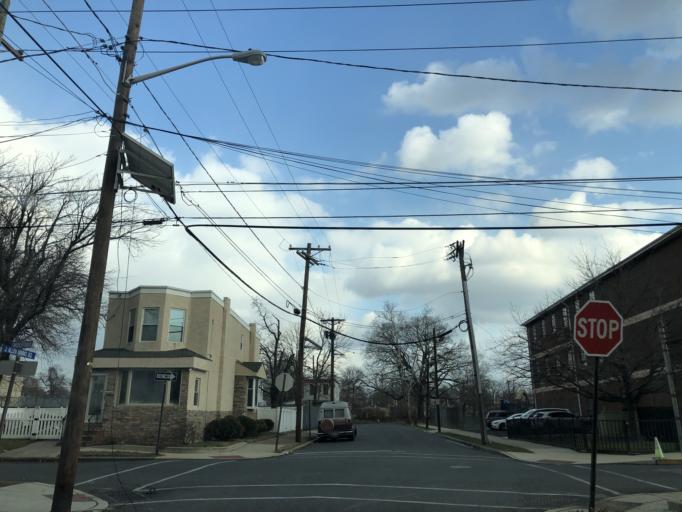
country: US
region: New Jersey
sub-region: Camden County
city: Wood-Lynne
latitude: 39.9208
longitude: -75.1080
